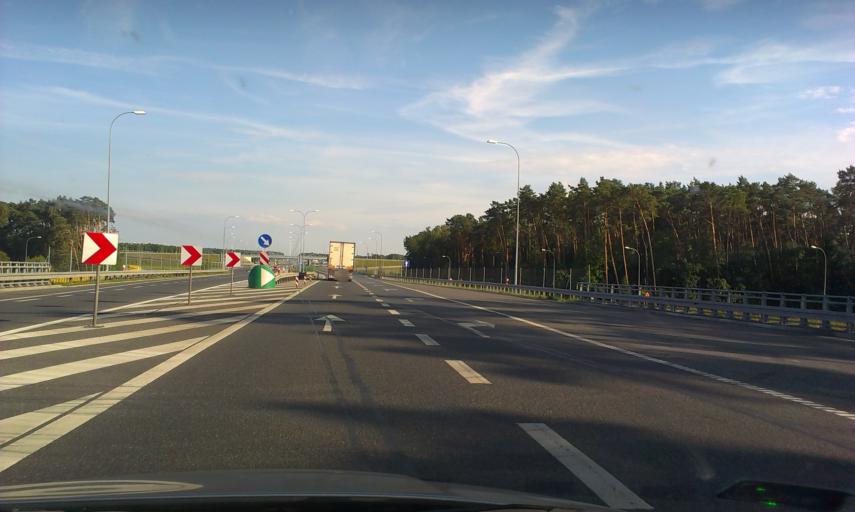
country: PL
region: Kujawsko-Pomorskie
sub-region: Powiat bydgoski
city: Biale Blota
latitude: 53.0999
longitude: 17.8919
